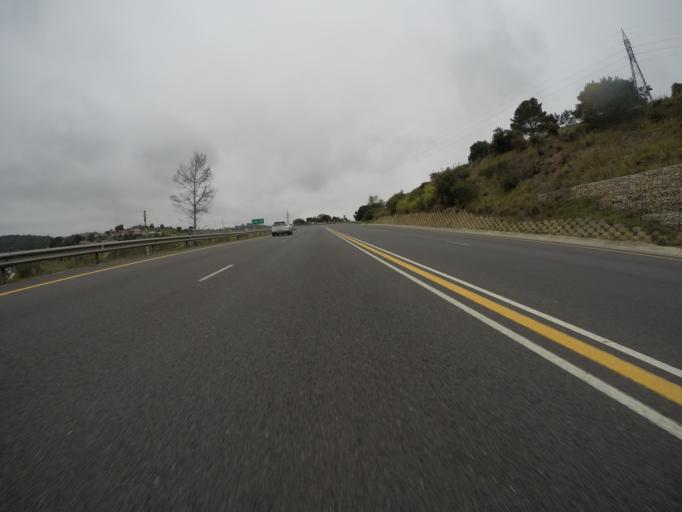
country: ZA
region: Western Cape
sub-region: Eden District Municipality
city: Knysna
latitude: -34.0444
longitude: 23.0898
